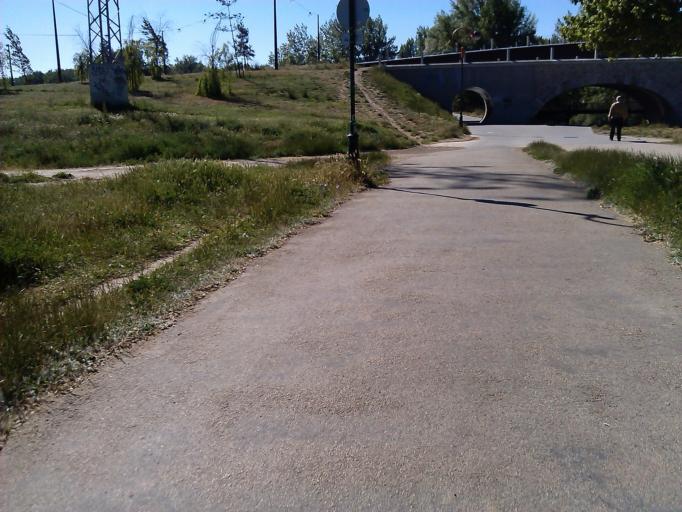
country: ES
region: Castille and Leon
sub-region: Provincia de Burgos
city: Burgos
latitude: 42.3432
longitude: -3.6651
